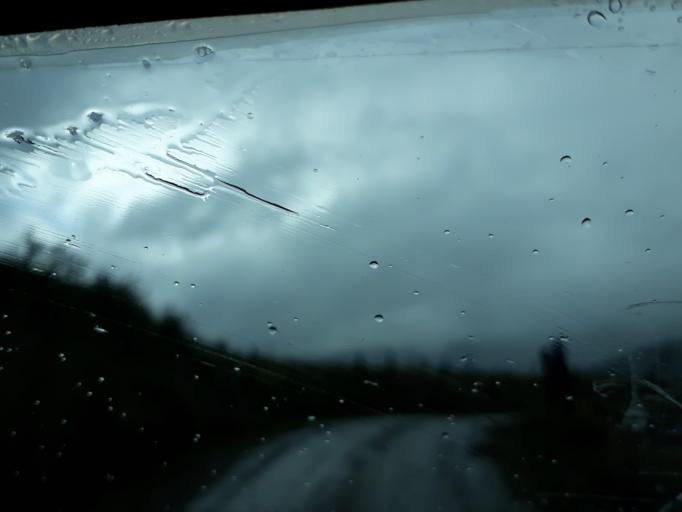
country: CO
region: Cundinamarca
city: La Mesa
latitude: 5.1704
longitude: -73.9179
